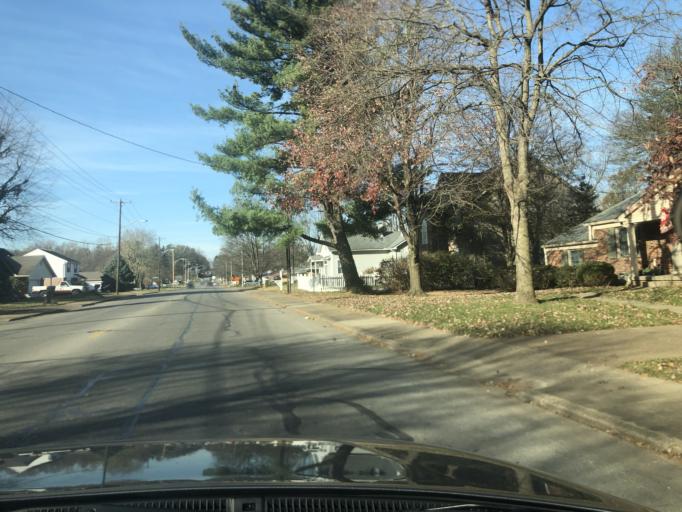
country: US
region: Indiana
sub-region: Warrick County
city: Newburgh
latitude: 37.9695
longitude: -87.4690
